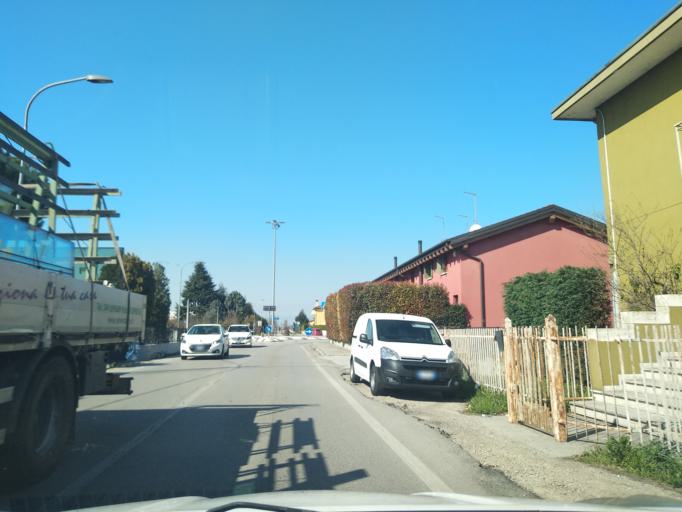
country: IT
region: Veneto
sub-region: Provincia di Padova
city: Taggi
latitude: 45.4737
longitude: 11.8122
